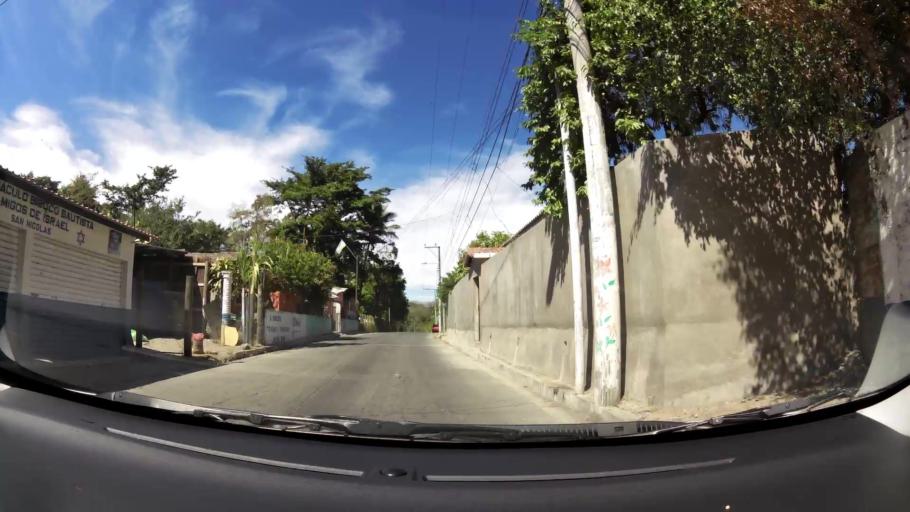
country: SV
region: San Salvador
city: Apopa
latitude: 13.8097
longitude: -89.1735
